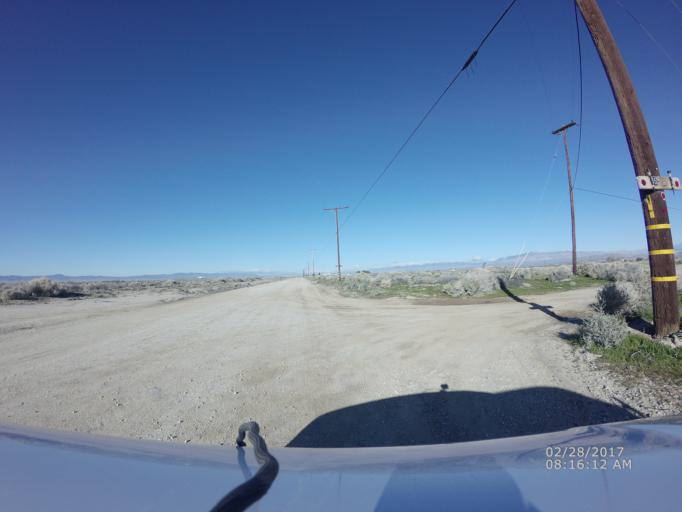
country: US
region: California
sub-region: Kern County
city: Rosamond
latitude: 34.8056
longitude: -118.2112
